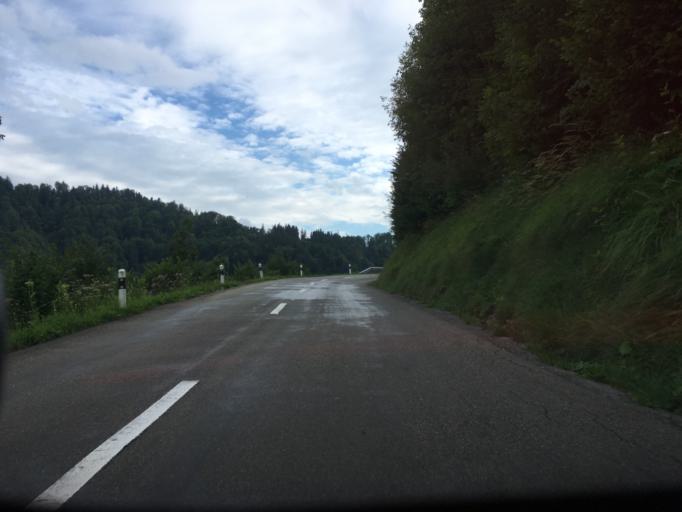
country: CH
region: Thurgau
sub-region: Muenchwilen District
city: Fischingen
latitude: 47.3688
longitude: 8.9752
